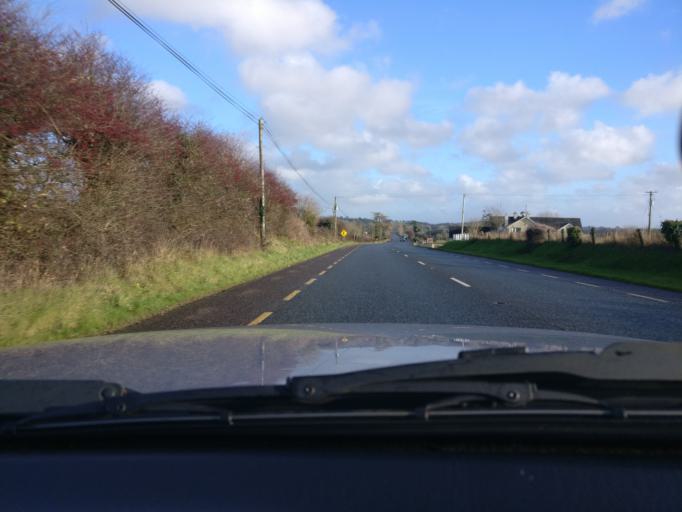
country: IE
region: Leinster
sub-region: Uibh Fhaili
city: Clara
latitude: 53.3987
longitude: -7.6150
